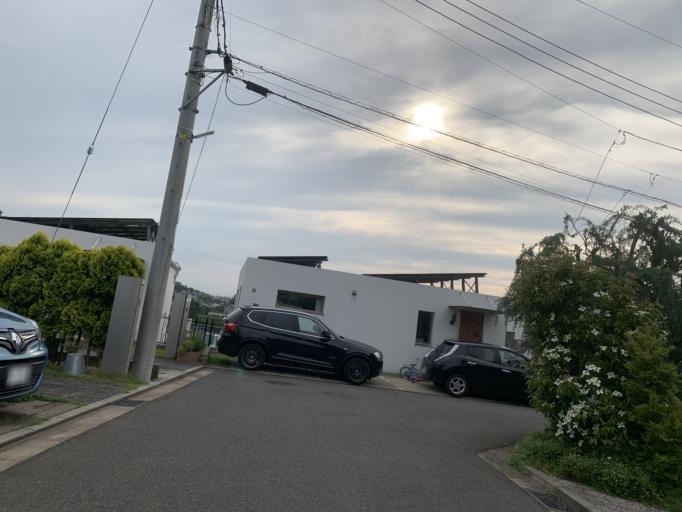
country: JP
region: Kanagawa
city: Yokohama
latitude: 35.5461
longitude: 139.5961
